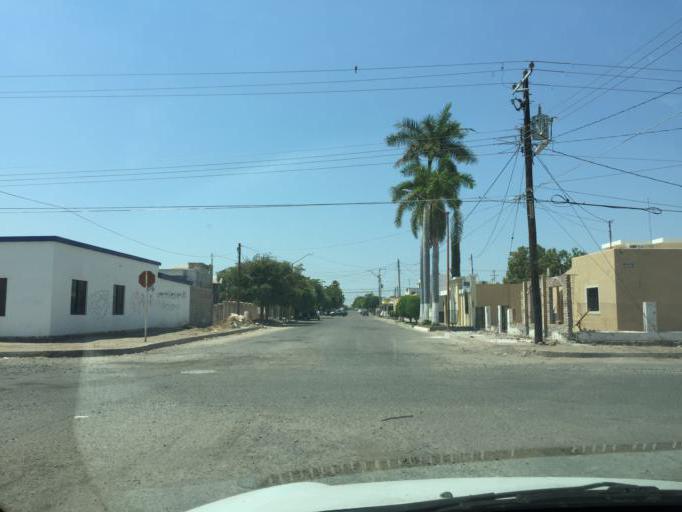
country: MX
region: Sonora
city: Navojoa
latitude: 27.0825
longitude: -109.4575
